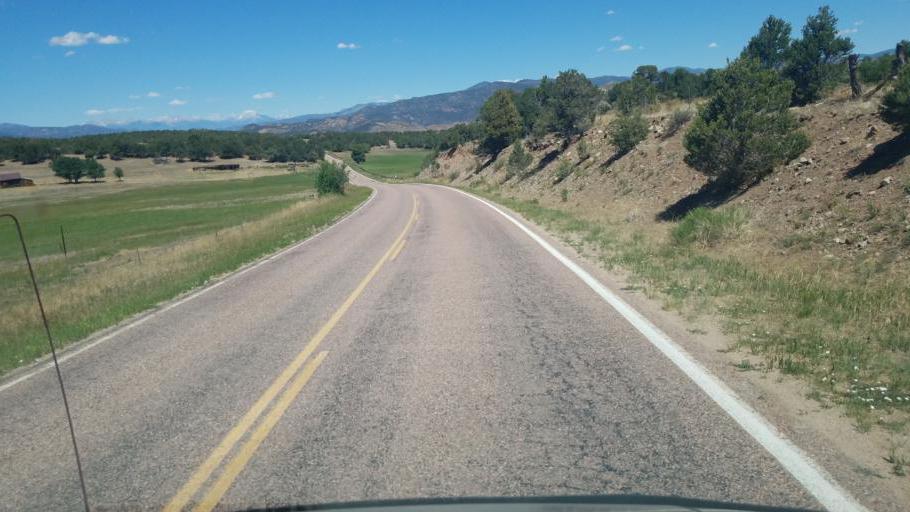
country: US
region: Colorado
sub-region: Custer County
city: Westcliffe
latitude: 38.3149
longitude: -105.6599
